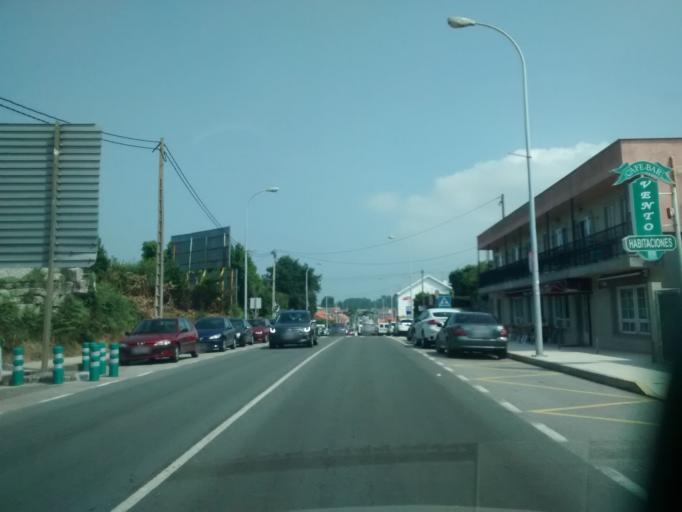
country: ES
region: Galicia
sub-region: Provincia de Pontevedra
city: Sanxenxo
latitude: 42.4079
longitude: -8.8126
